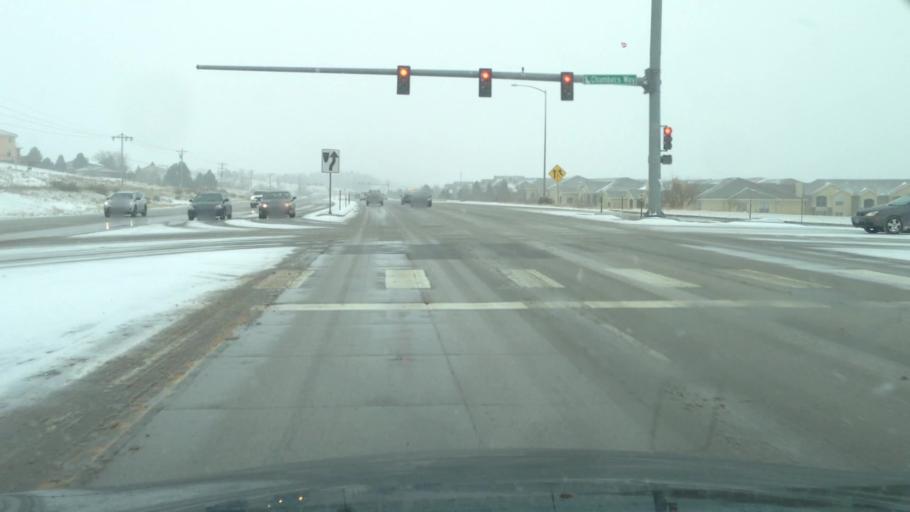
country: US
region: Colorado
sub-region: Arapahoe County
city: Dove Valley
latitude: 39.5883
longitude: -104.7984
